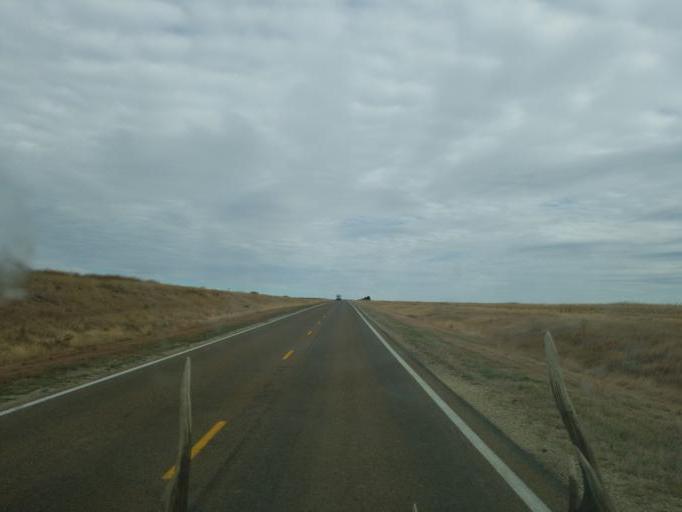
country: US
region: Kansas
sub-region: Wallace County
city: Sharon Springs
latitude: 39.0236
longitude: -101.3291
